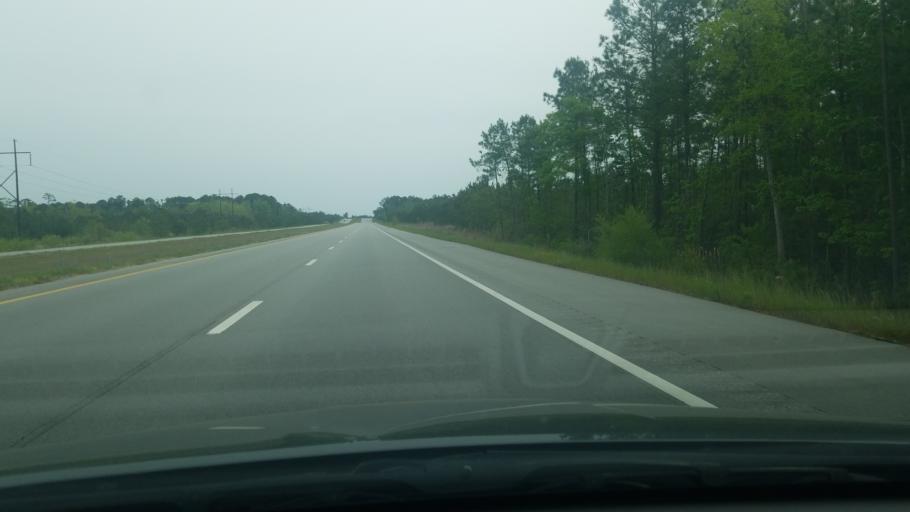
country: US
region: North Carolina
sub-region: Craven County
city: River Bend
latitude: 35.0446
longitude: -77.2184
